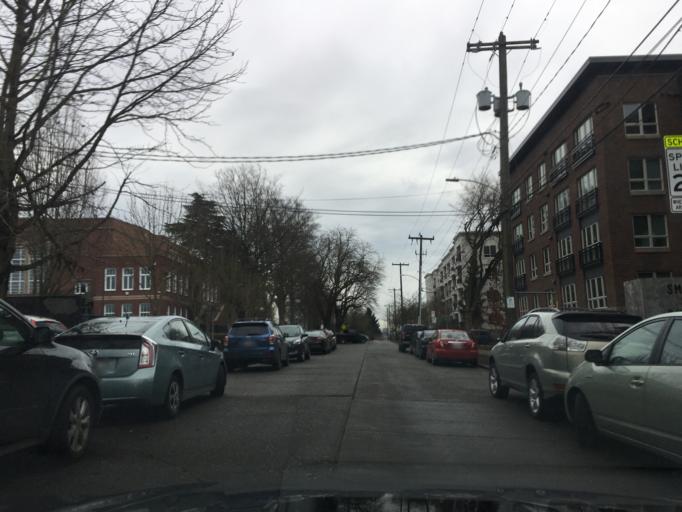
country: US
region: Washington
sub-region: King County
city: Seattle
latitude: 47.6612
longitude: -122.3407
